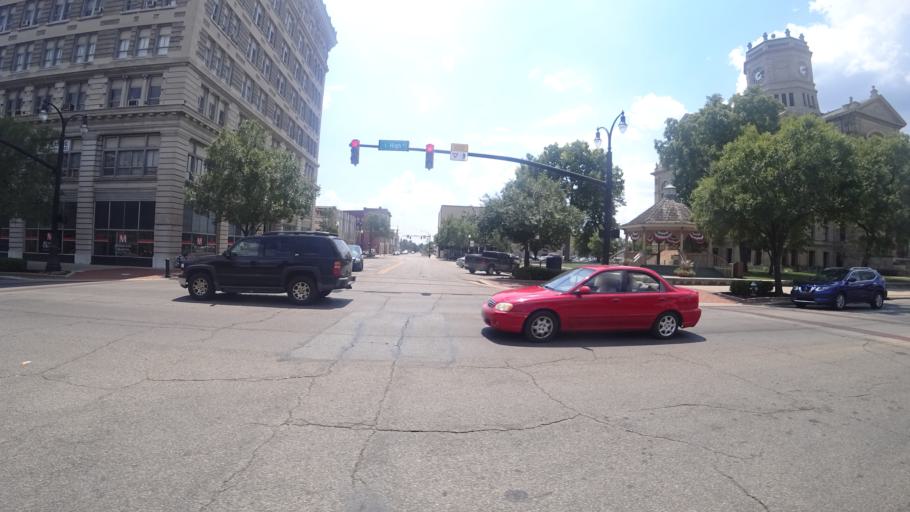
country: US
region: Ohio
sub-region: Butler County
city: Hamilton
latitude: 39.3998
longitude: -84.5619
